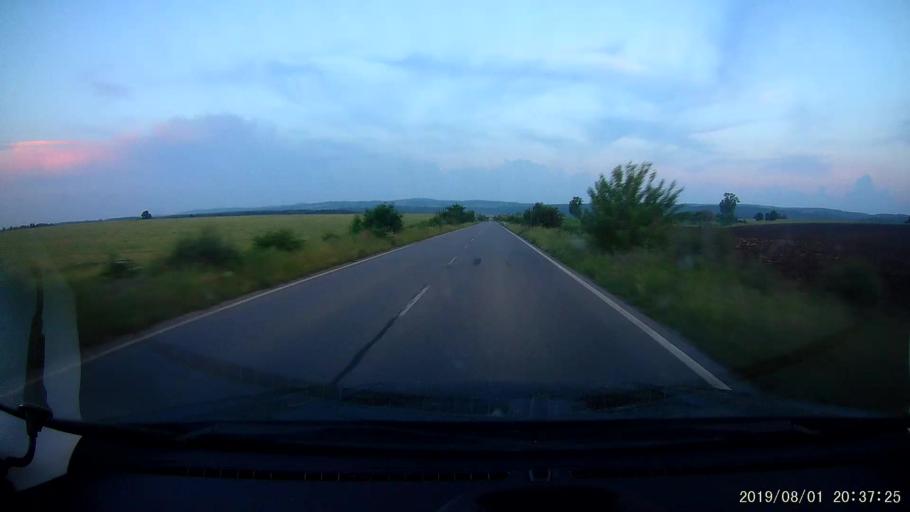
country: BG
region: Yambol
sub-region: Obshtina Elkhovo
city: Elkhovo
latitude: 42.0487
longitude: 26.5941
